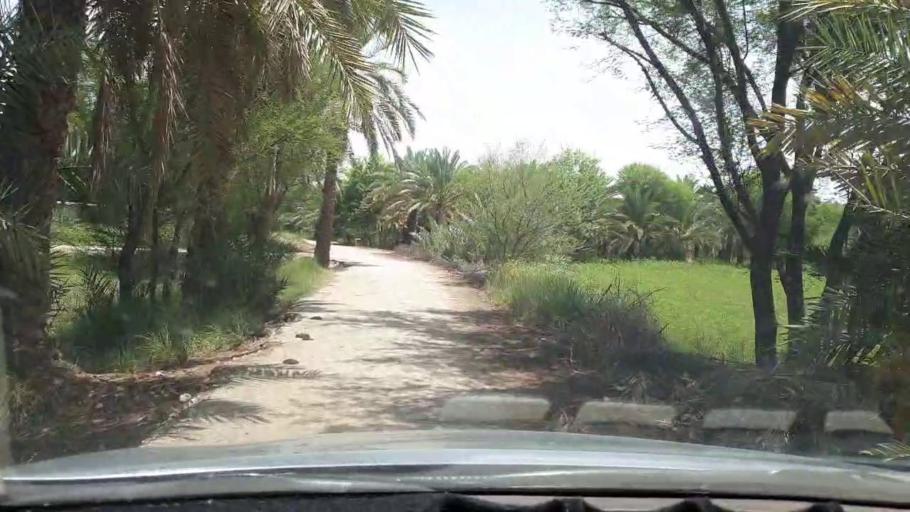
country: PK
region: Sindh
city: Khairpur
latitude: 27.4507
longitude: 68.7801
